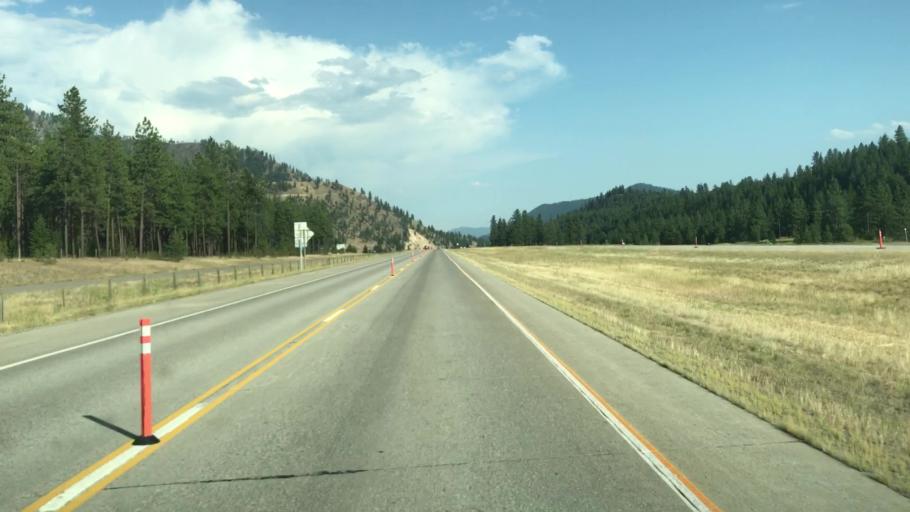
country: US
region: Montana
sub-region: Mineral County
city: Superior
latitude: 47.2326
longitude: -114.9836
